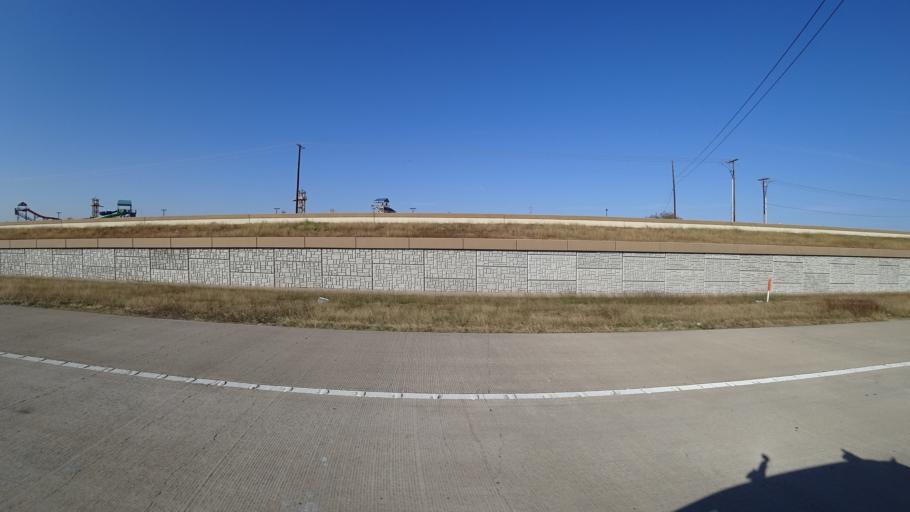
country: US
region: Texas
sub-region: Travis County
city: Pflugerville
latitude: 30.4623
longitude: -97.5947
